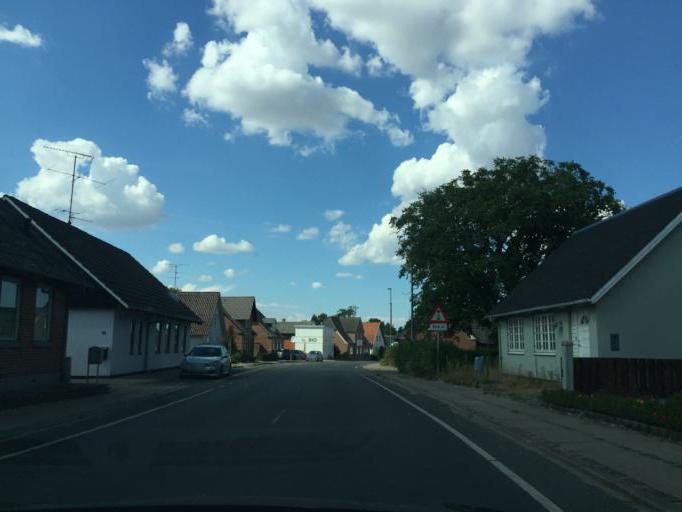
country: DK
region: South Denmark
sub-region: Assens Kommune
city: Harby
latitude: 55.2220
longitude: 10.1213
